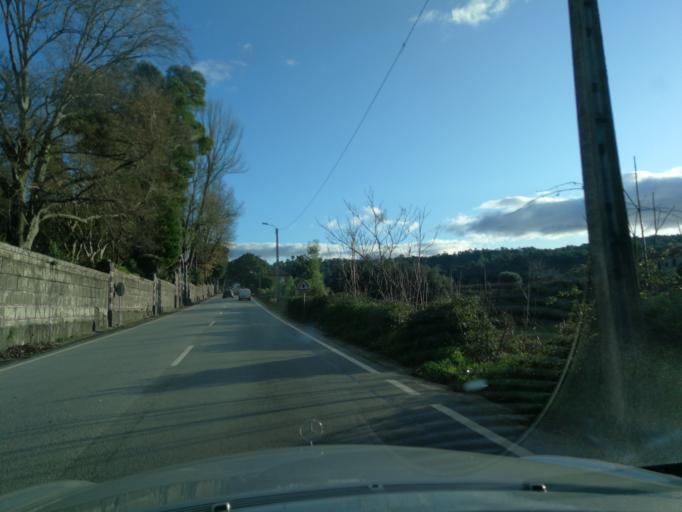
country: PT
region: Braga
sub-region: Esposende
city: Marinhas
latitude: 41.6015
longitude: -8.7403
